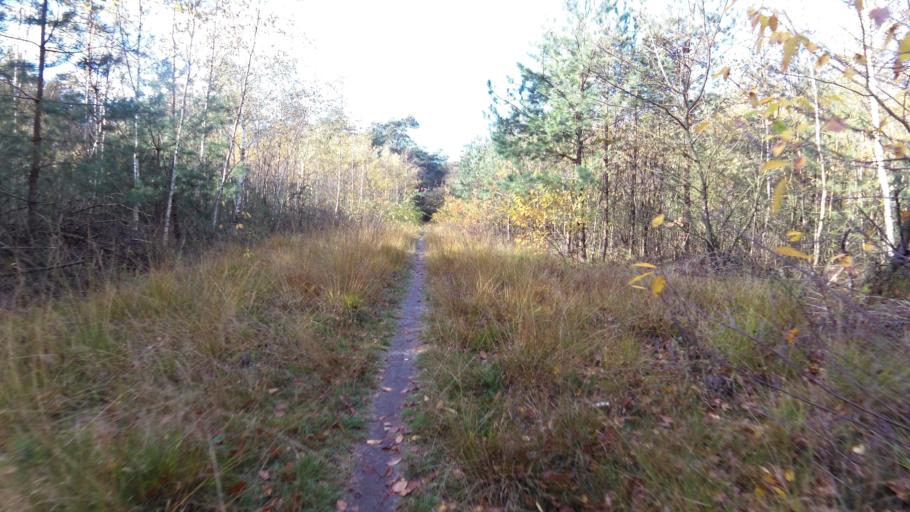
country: NL
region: Gelderland
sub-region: Gemeente Nunspeet
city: Nunspeet
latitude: 52.3565
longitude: 5.8095
